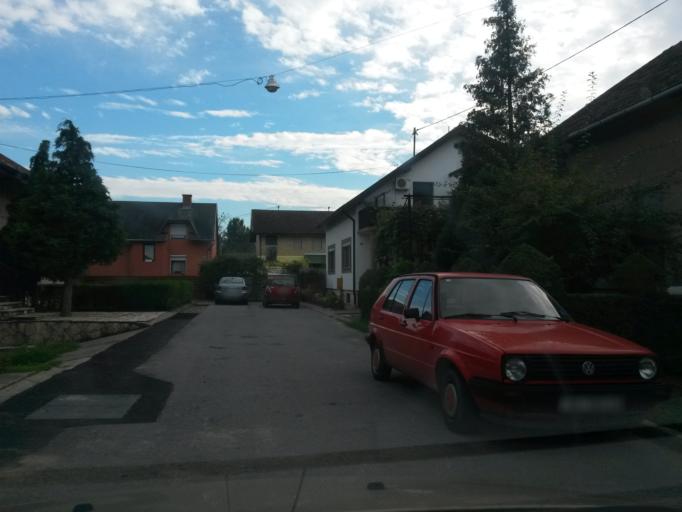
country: HR
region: Osjecko-Baranjska
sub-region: Grad Osijek
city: Osijek
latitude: 45.5543
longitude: 18.7378
